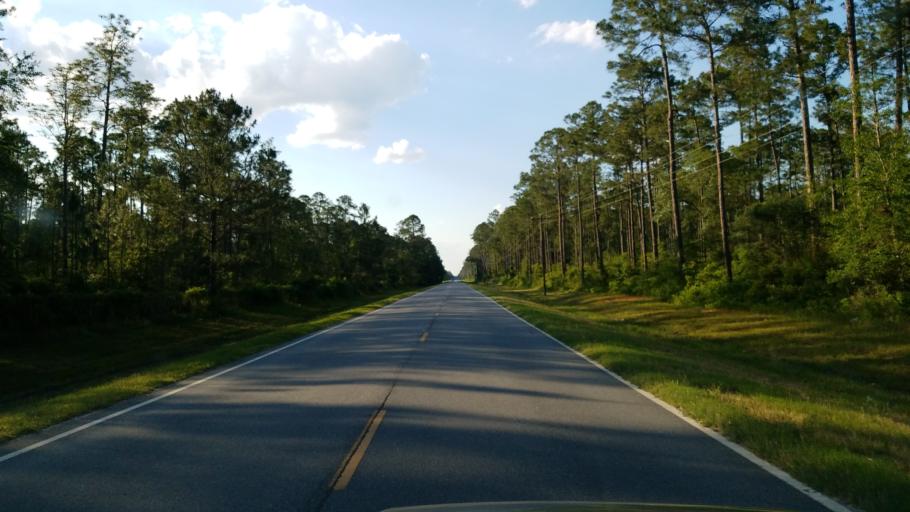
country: US
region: Georgia
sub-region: Lanier County
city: Lakeland
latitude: 31.0898
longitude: -83.0771
